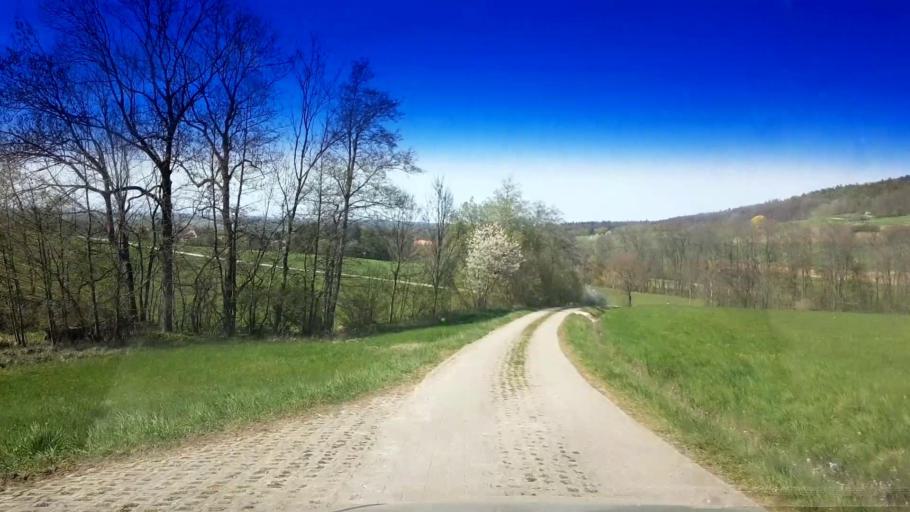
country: DE
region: Bavaria
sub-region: Upper Franconia
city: Schesslitz
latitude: 49.9444
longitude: 11.0445
